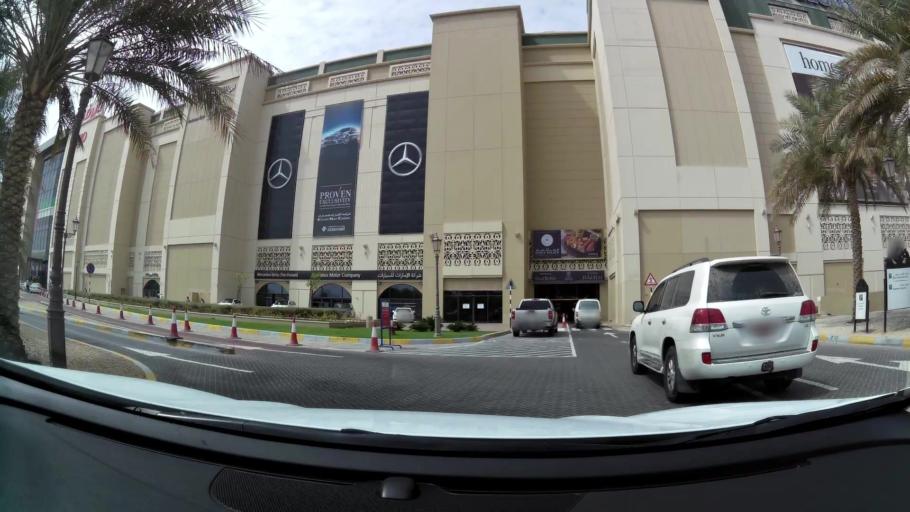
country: AE
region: Abu Dhabi
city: Abu Dhabi
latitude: 24.5240
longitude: 54.6724
